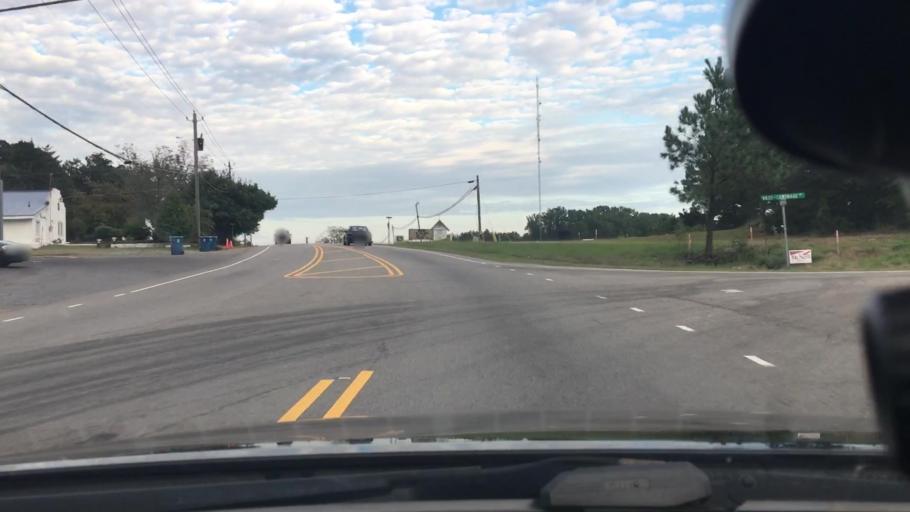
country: US
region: North Carolina
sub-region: Moore County
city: Carthage
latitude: 35.3412
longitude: -79.4088
